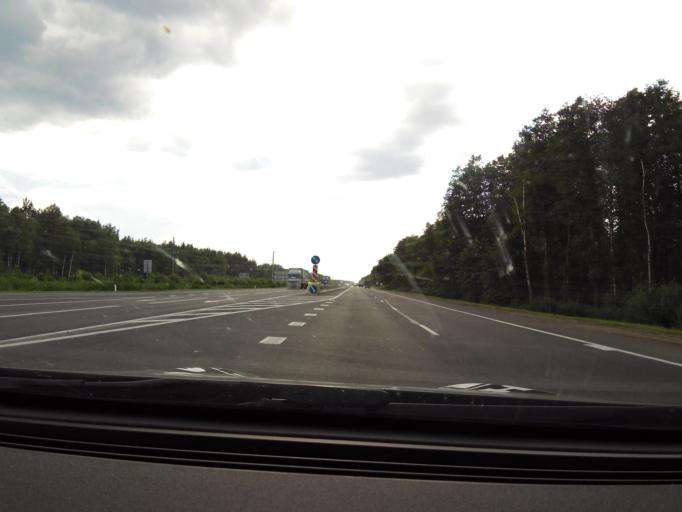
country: RU
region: Nizjnij Novgorod
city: Volodarsk
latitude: 56.2850
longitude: 43.1643
